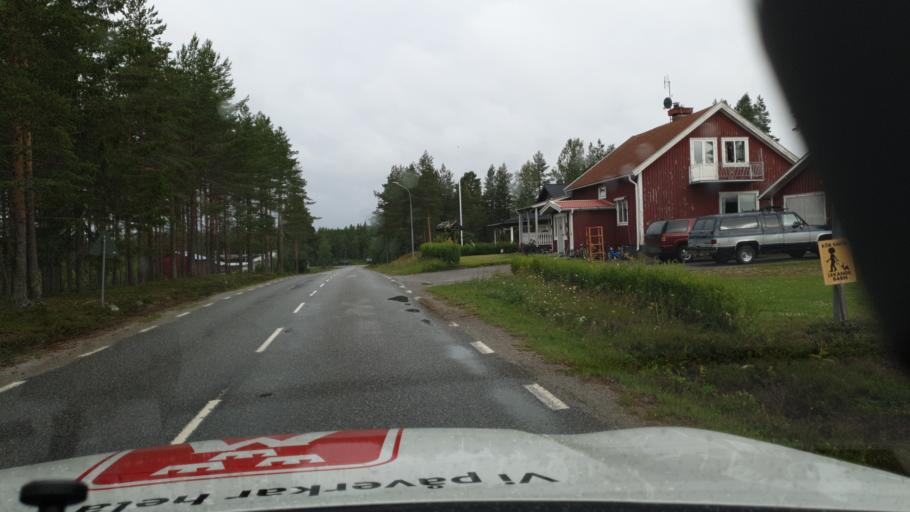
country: SE
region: Vaesterbotten
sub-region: Umea Kommun
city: Saevar
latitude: 64.0240
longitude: 20.4829
